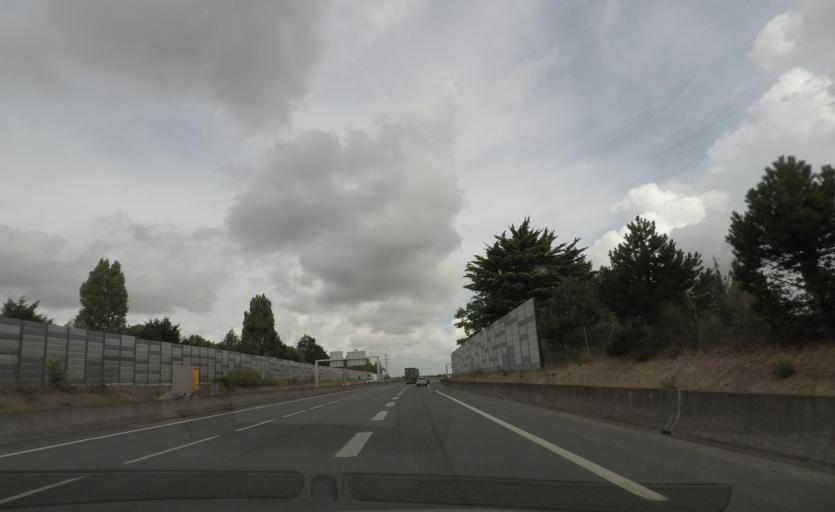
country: FR
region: Pays de la Loire
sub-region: Departement de Maine-et-Loire
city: Ecouflant
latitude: 47.4979
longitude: -0.5004
